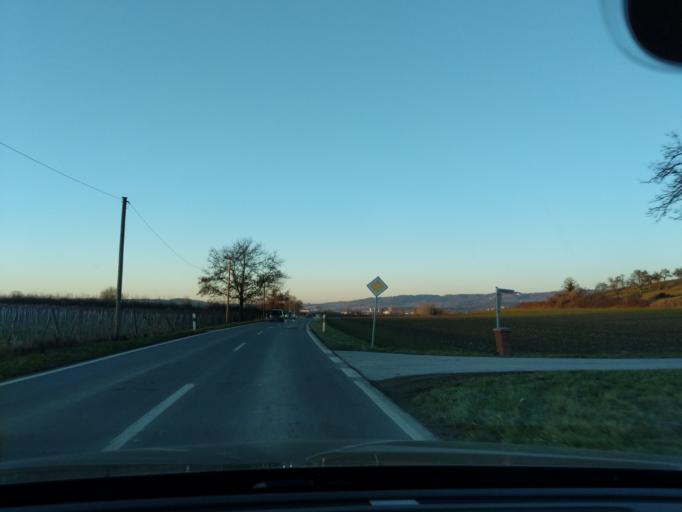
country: DE
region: Baden-Wuerttemberg
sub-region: Tuebingen Region
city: Salem
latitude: 47.7350
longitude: 9.3125
